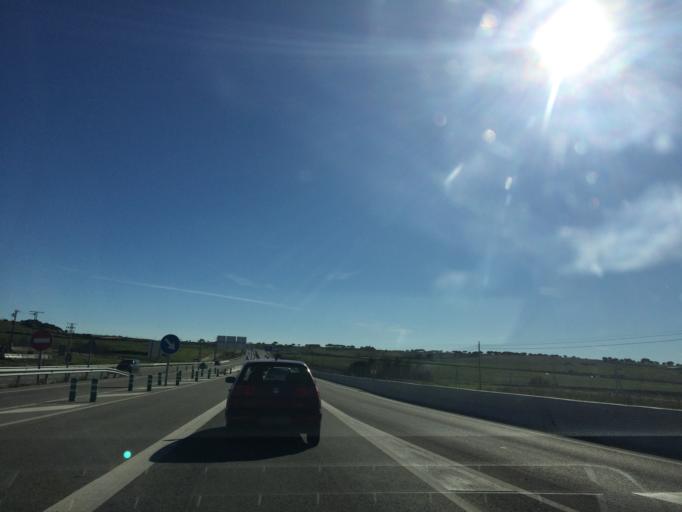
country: ES
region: Madrid
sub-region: Provincia de Madrid
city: Colmenar Viejo
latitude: 40.7124
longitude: -3.7939
